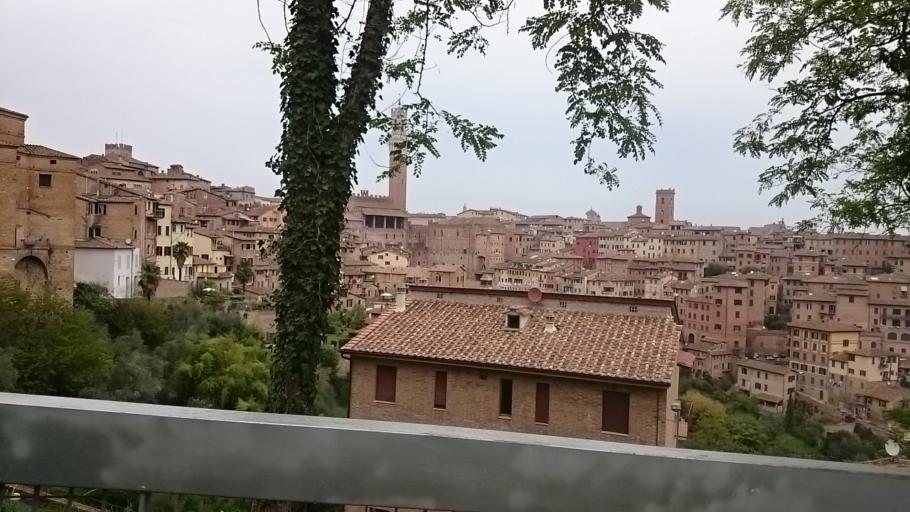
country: IT
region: Tuscany
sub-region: Provincia di Siena
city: Siena
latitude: 43.3147
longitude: 11.3326
